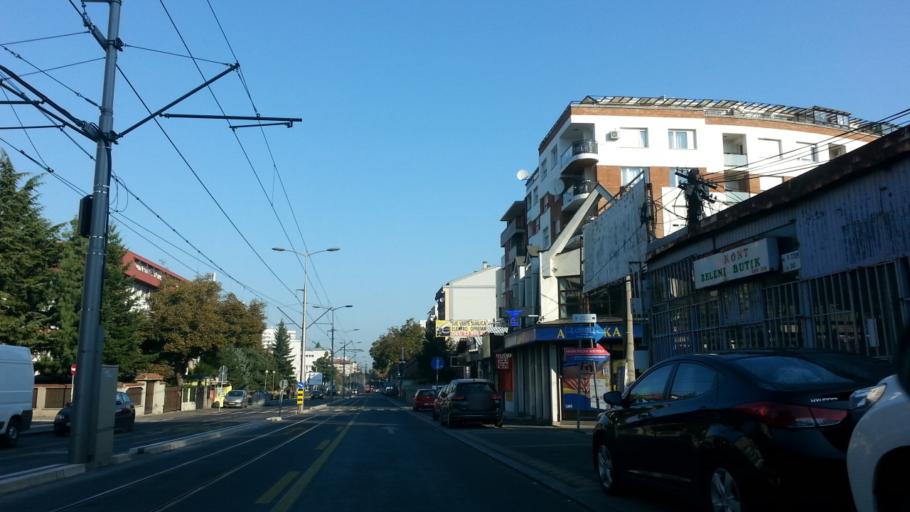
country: RS
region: Central Serbia
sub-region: Belgrade
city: Vozdovac
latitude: 44.7623
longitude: 20.4840
